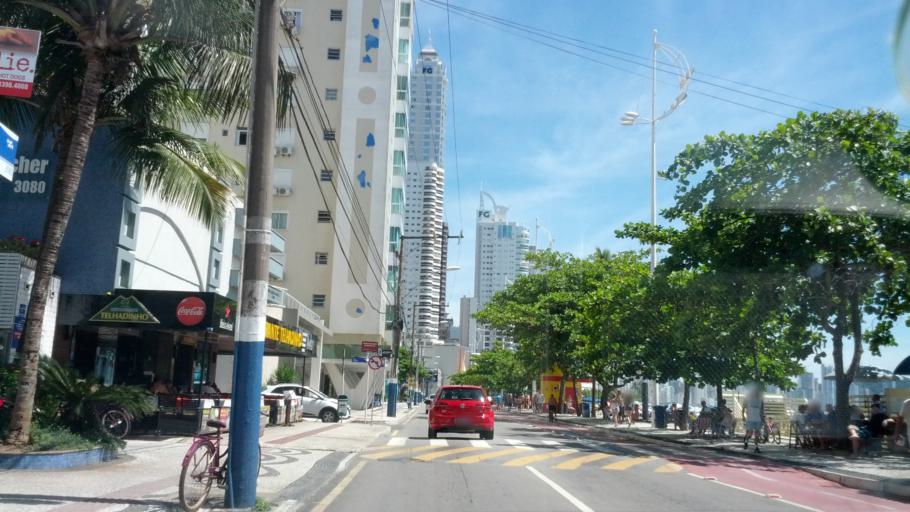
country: BR
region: Santa Catarina
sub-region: Balneario Camboriu
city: Balneario Camboriu
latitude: -26.9955
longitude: -48.6265
